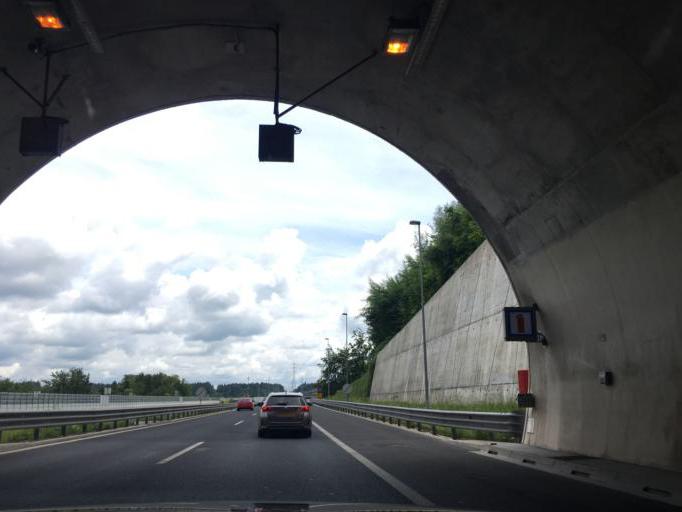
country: SI
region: Trzic
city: Bistrica pri Trzicu
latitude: 46.3183
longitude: 14.2439
